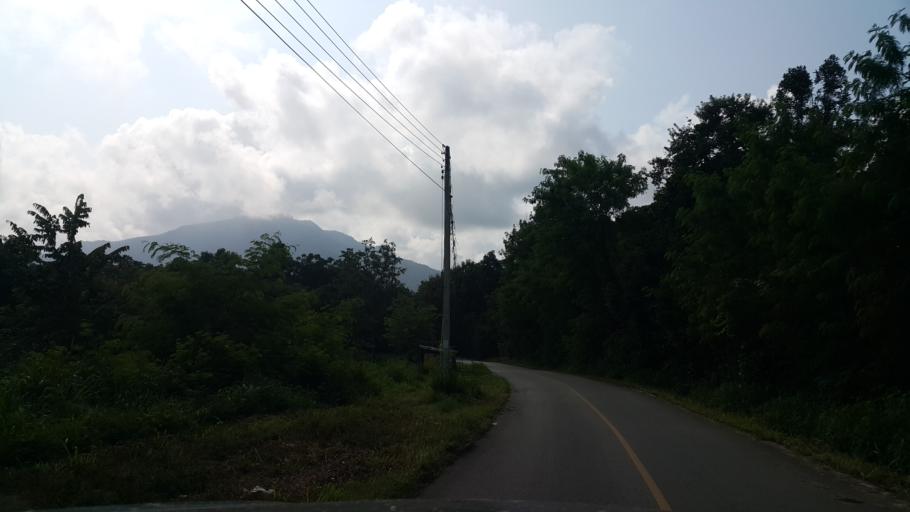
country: TH
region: Chiang Mai
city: Mae On
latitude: 18.7461
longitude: 99.2212
